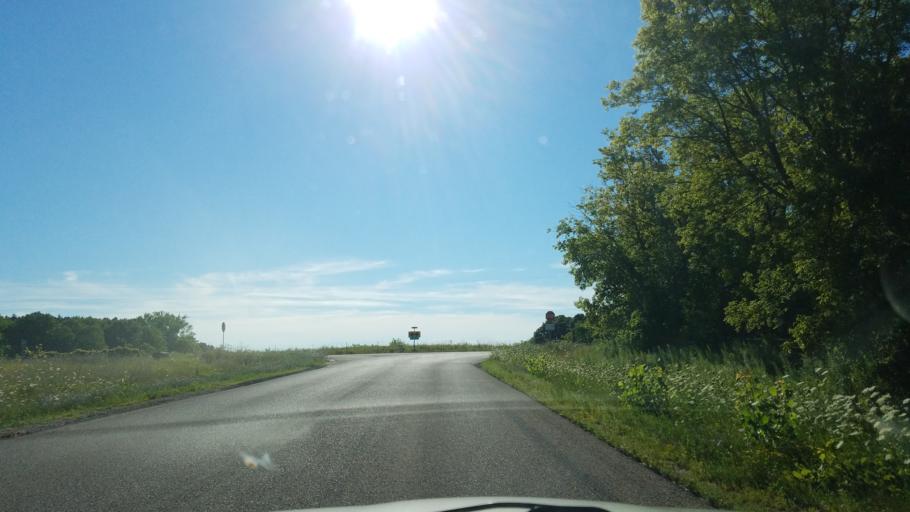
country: US
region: Wisconsin
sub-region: Saint Croix County
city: Somerset
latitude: 45.1110
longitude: -92.7258
